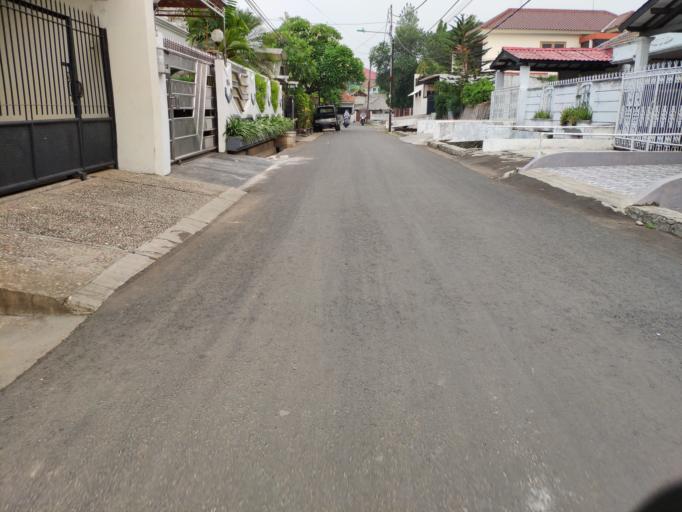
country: ID
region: Jakarta Raya
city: Jakarta
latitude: -6.2008
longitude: 106.8664
